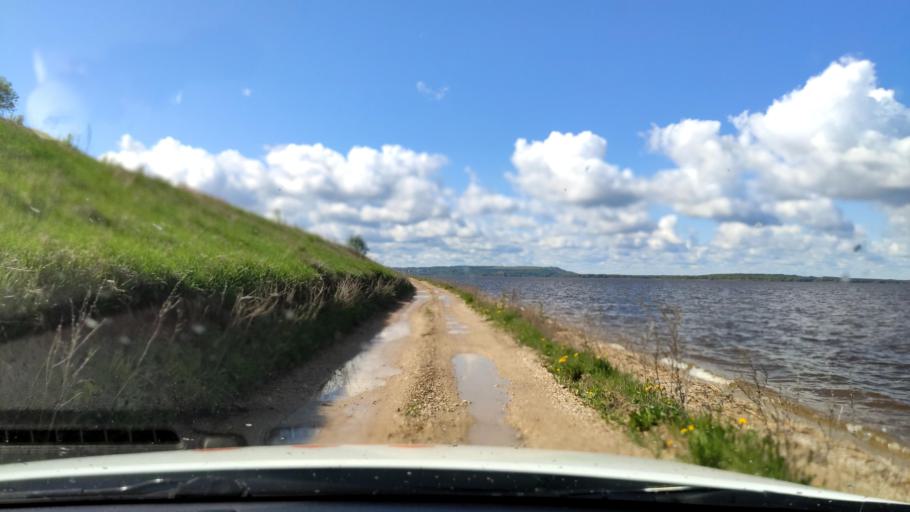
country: RU
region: Tatarstan
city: Sviyazhsk
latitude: 55.7741
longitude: 48.6892
